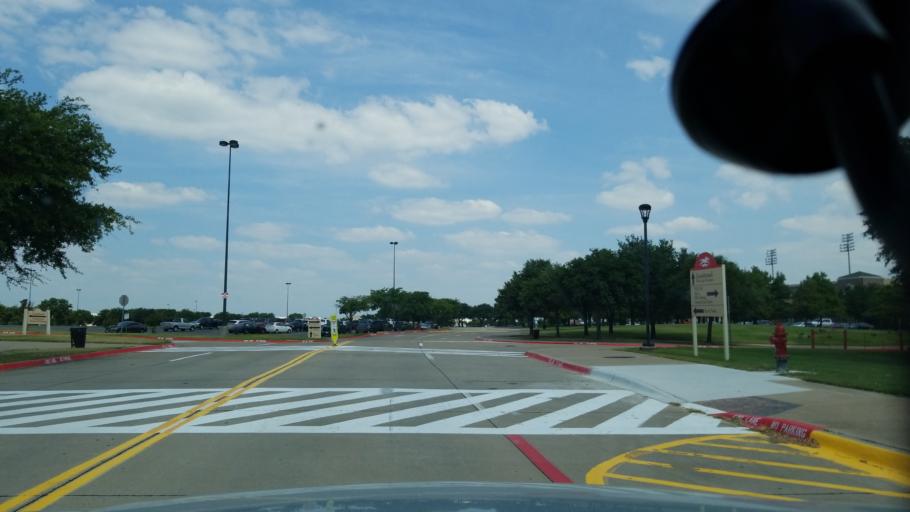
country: US
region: Texas
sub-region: Dallas County
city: Grand Prairie
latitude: 32.7716
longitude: -96.9894
